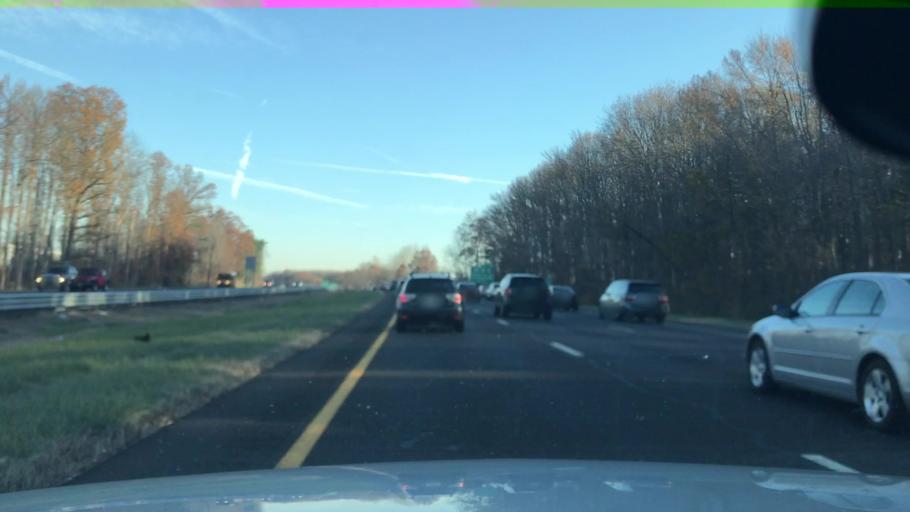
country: US
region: New Jersey
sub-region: Burlington County
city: Bordentown
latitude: 40.1183
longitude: -74.7219
